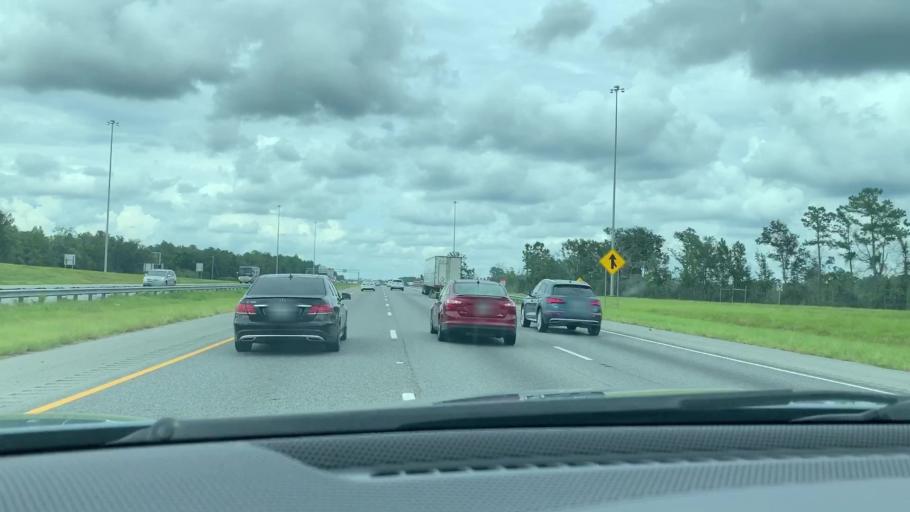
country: US
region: Georgia
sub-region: McIntosh County
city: Darien
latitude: 31.3975
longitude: -81.4483
